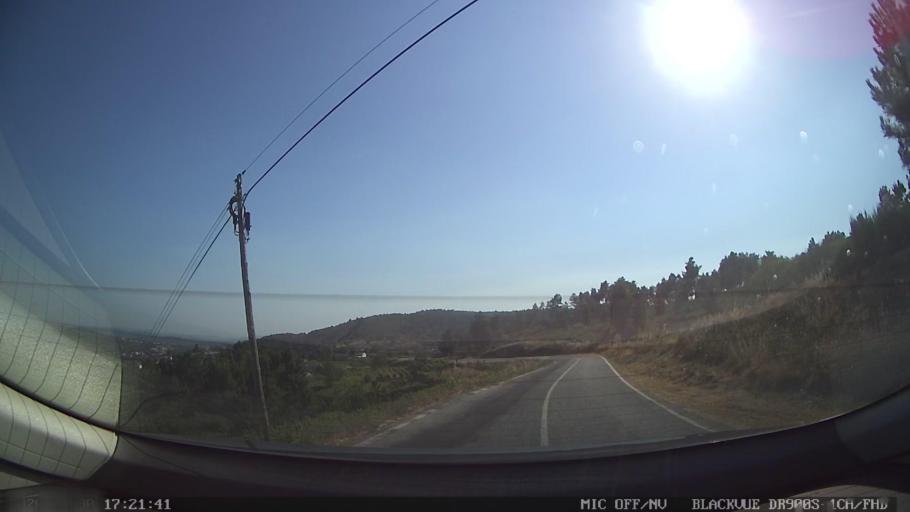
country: PT
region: Vila Real
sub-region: Sabrosa
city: Sabrosa
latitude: 41.2997
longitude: -7.4762
